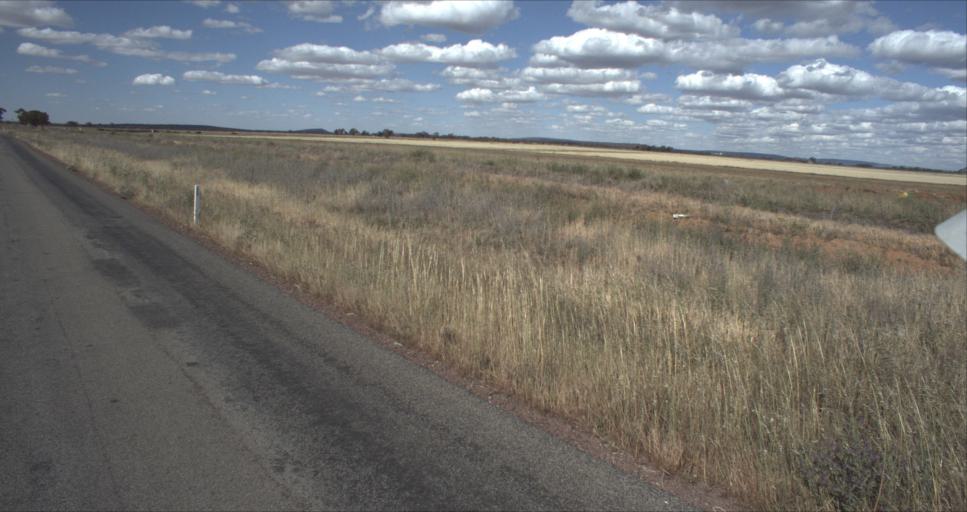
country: AU
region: New South Wales
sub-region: Leeton
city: Leeton
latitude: -34.4233
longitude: 146.2632
